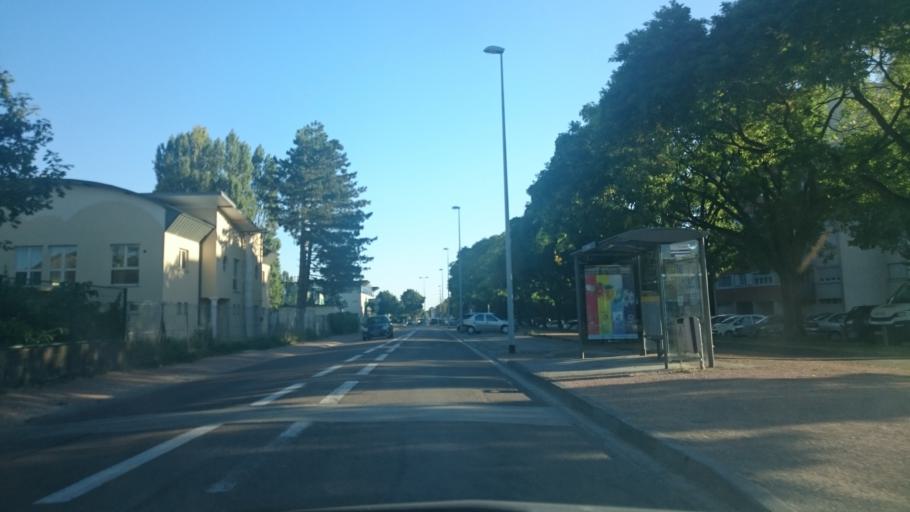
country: FR
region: Bourgogne
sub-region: Departement de la Cote-d'Or
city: Saint-Apollinaire
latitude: 47.3458
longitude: 5.0591
